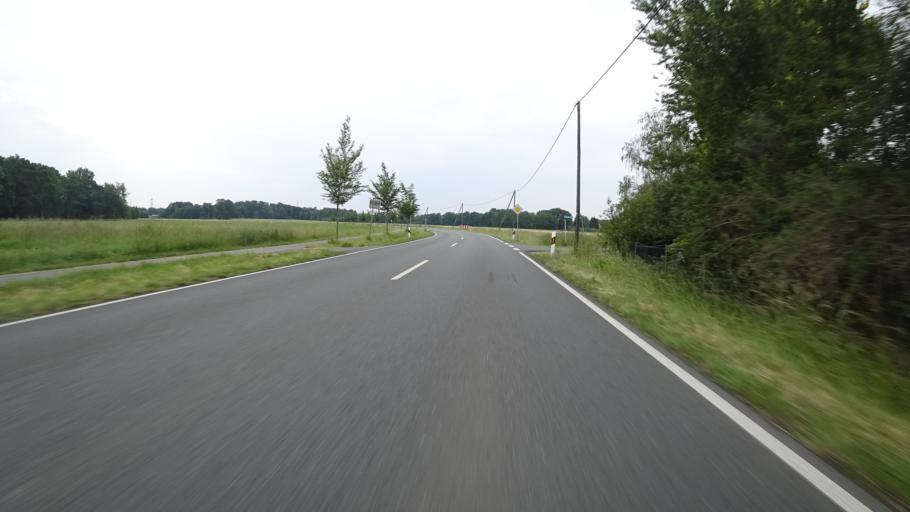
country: DE
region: North Rhine-Westphalia
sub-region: Regierungsbezirk Detmold
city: Guetersloh
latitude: 51.9413
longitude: 8.3804
